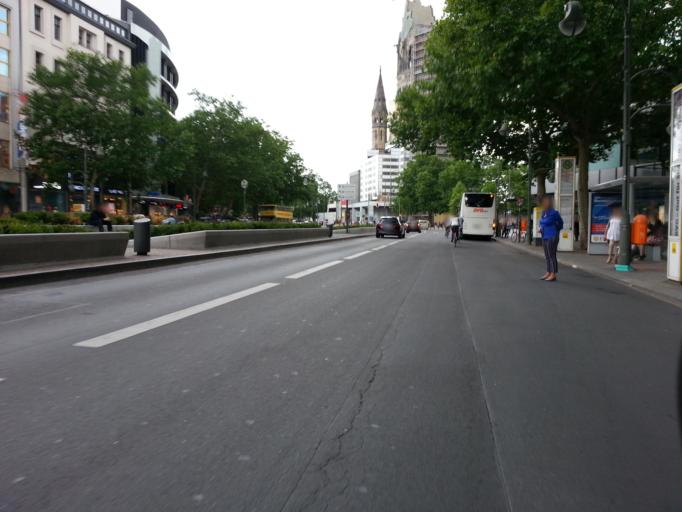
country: DE
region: Berlin
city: Hansaviertel
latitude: 52.5035
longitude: 13.3377
